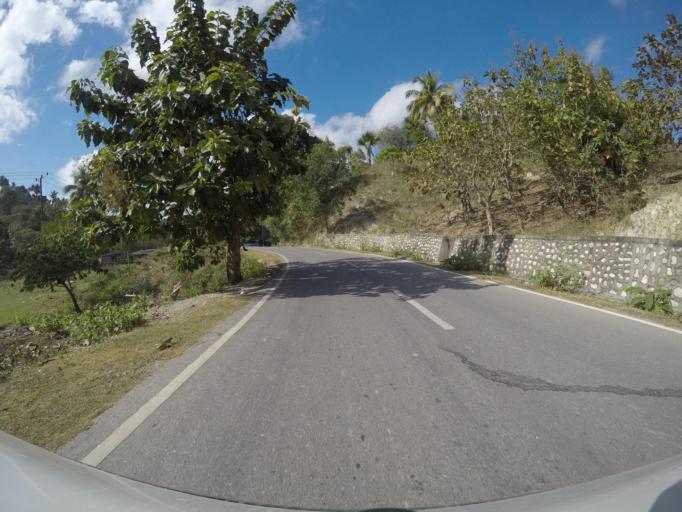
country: TL
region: Viqueque
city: Viqueque
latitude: -8.8783
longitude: 126.3757
